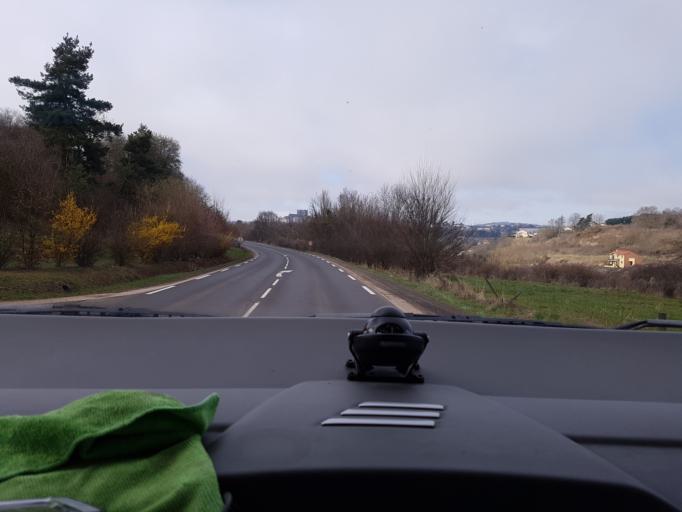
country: FR
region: Auvergne
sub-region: Departement du Cantal
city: Saint-Flour
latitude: 45.0425
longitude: 3.1066
